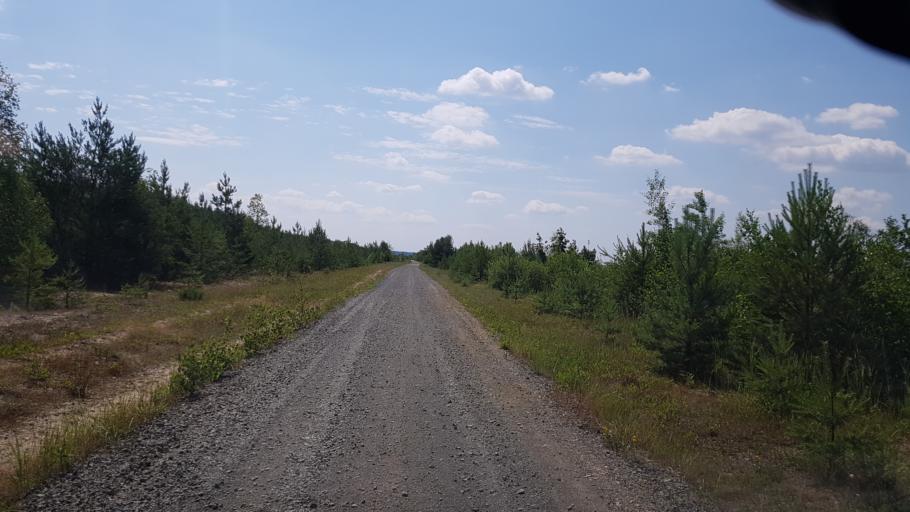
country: DE
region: Brandenburg
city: Sallgast
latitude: 51.5780
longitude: 13.8012
